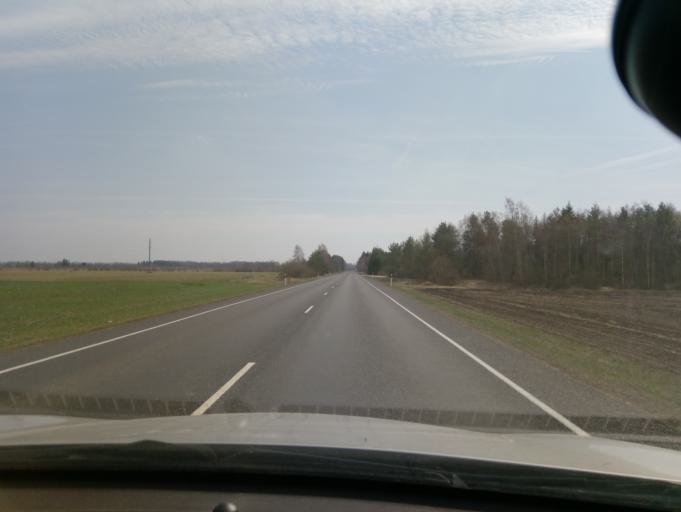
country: EE
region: Viljandimaa
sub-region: Vohma linn
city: Vohma
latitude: 58.7465
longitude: 25.5738
